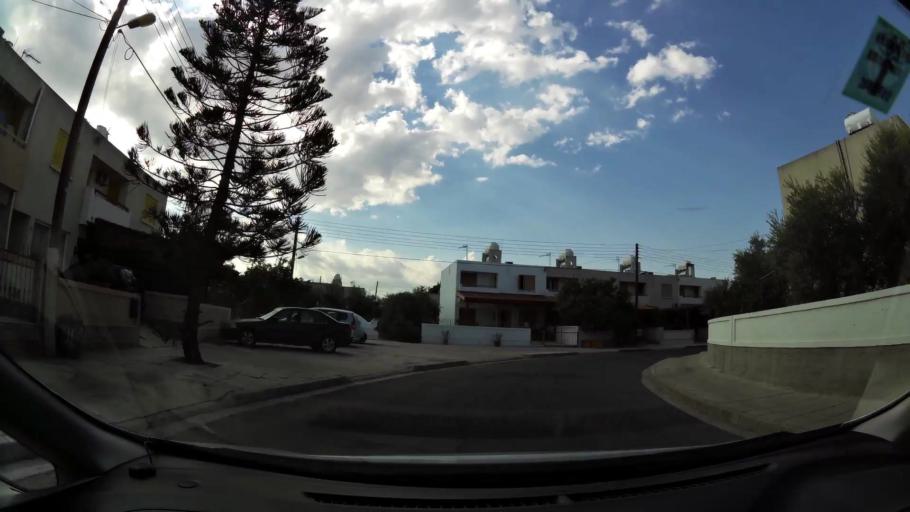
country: CY
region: Larnaka
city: Livadia
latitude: 34.9399
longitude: 33.6136
